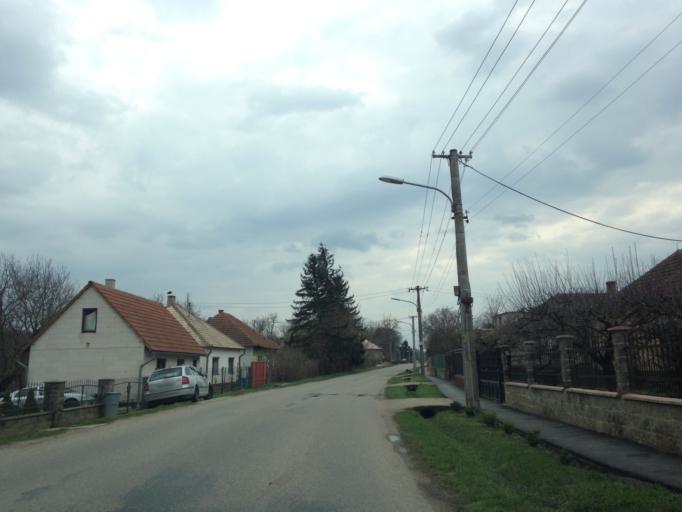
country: SK
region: Nitriansky
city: Svodin
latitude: 47.9623
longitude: 18.4108
